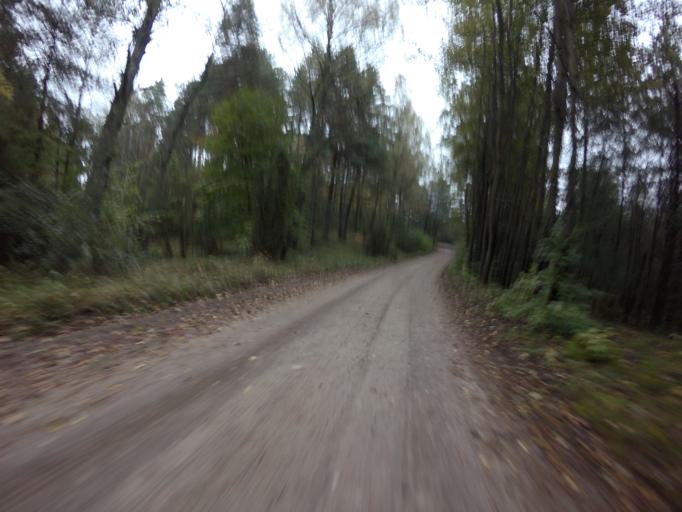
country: PL
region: Pomeranian Voivodeship
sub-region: Powiat kartuski
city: Stezyca
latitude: 54.1604
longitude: 17.9215
